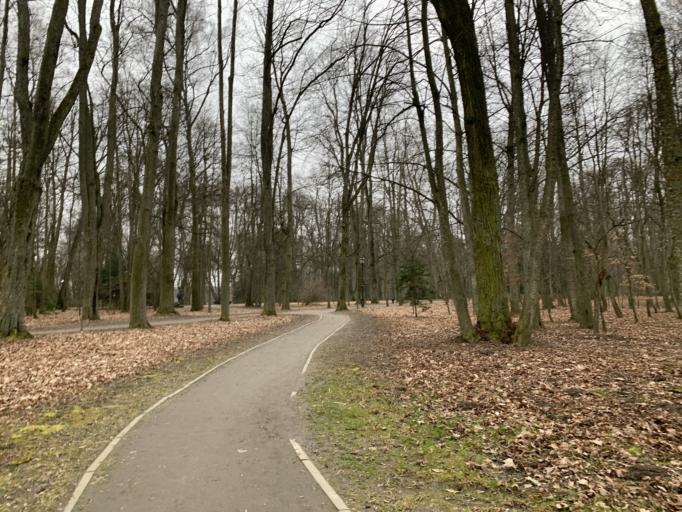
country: BY
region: Minsk
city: Nyasvizh
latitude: 53.2275
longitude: 26.6925
